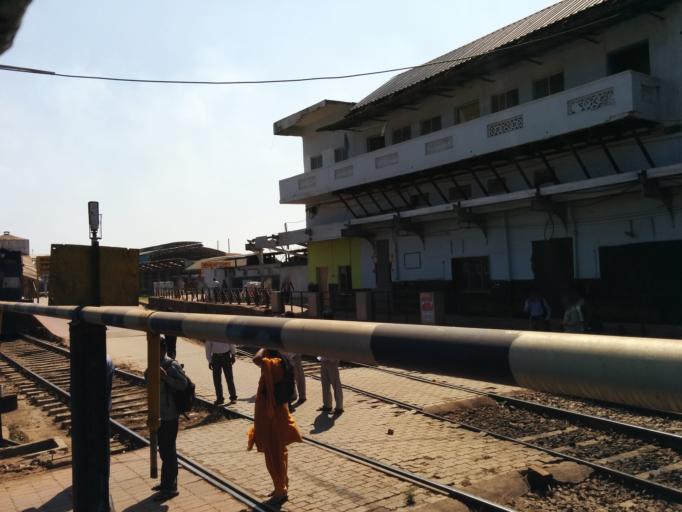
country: IN
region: Karnataka
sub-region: Dharwad
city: Hubli
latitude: 15.3520
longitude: 75.1473
